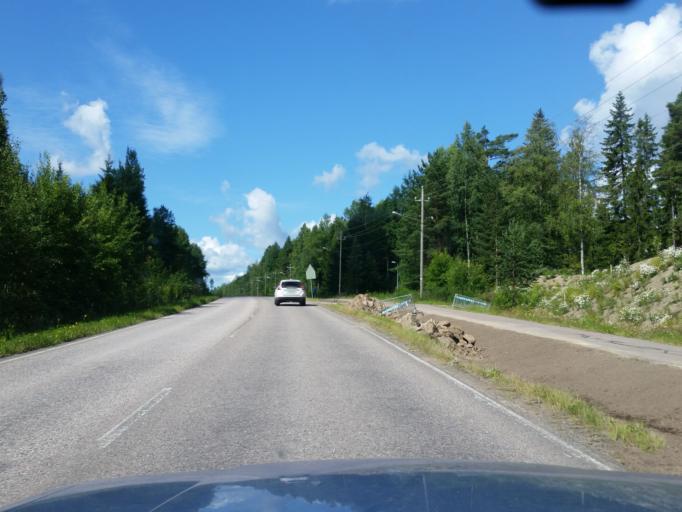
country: FI
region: Uusimaa
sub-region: Helsinki
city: Vihti
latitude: 60.3270
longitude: 24.3021
